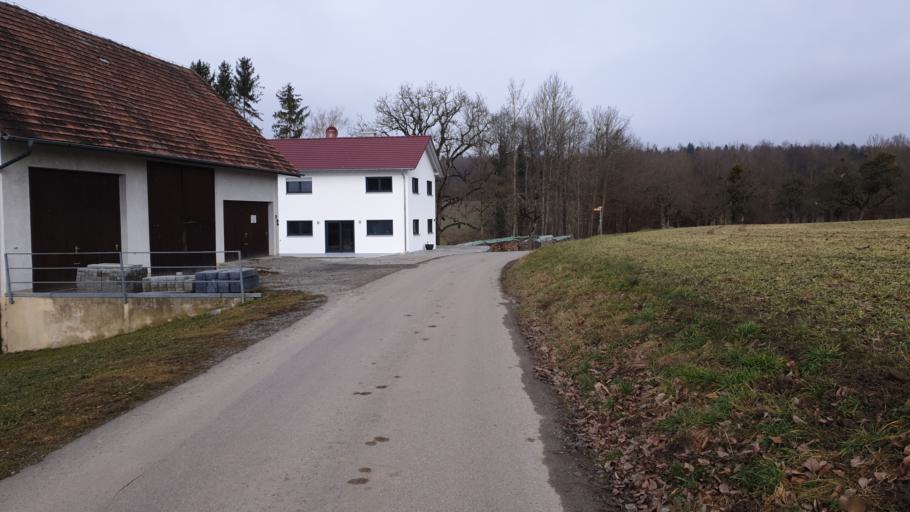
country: DE
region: Baden-Wuerttemberg
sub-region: Tuebingen Region
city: Wolpertswende
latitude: 47.8804
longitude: 9.6308
